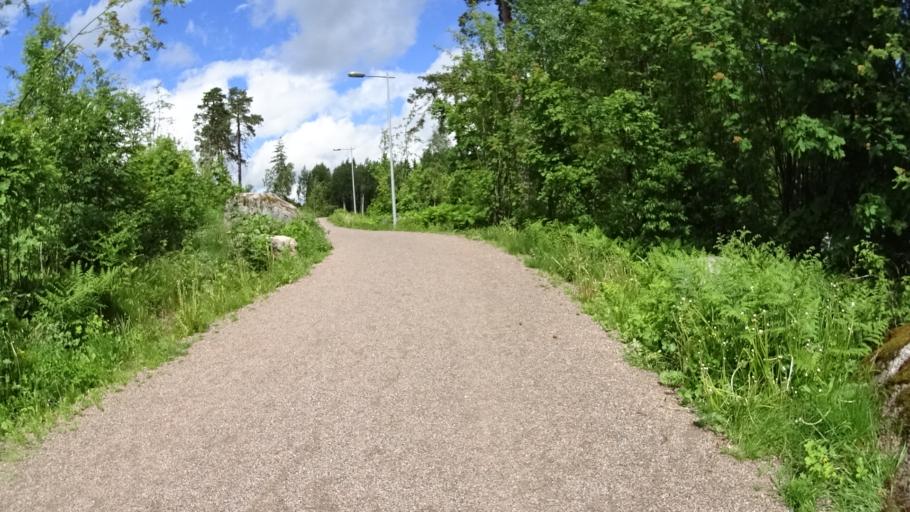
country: FI
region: Uusimaa
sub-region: Helsinki
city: Kilo
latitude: 60.2401
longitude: 24.8244
